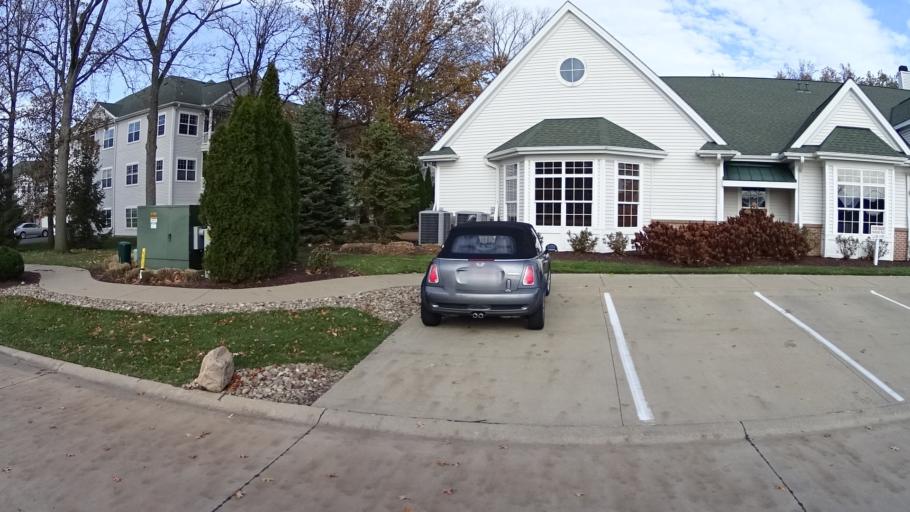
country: US
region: Ohio
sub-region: Lorain County
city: Sheffield Lake
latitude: 41.4961
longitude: -82.0651
